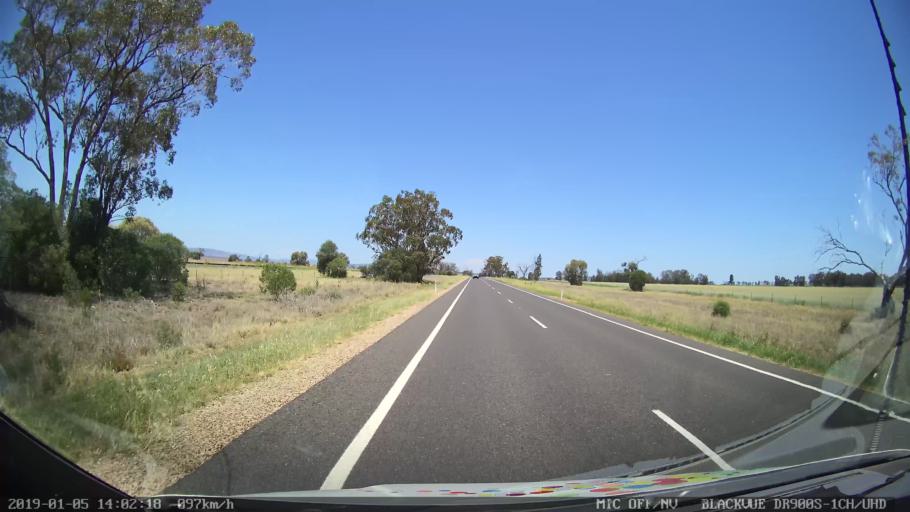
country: AU
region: New South Wales
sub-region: Gunnedah
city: Gunnedah
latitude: -31.1784
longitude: 150.3361
